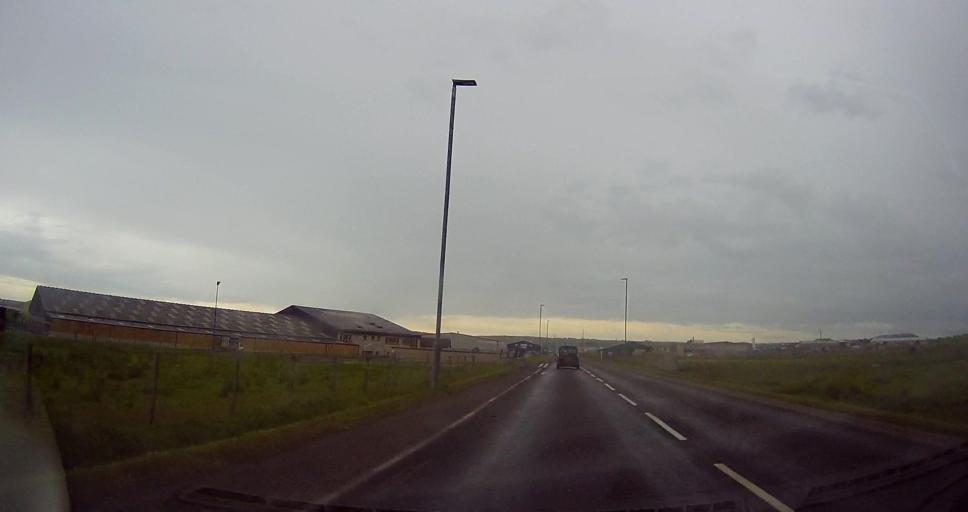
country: GB
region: Scotland
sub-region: Orkney Islands
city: Orkney
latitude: 58.9955
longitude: -2.9820
